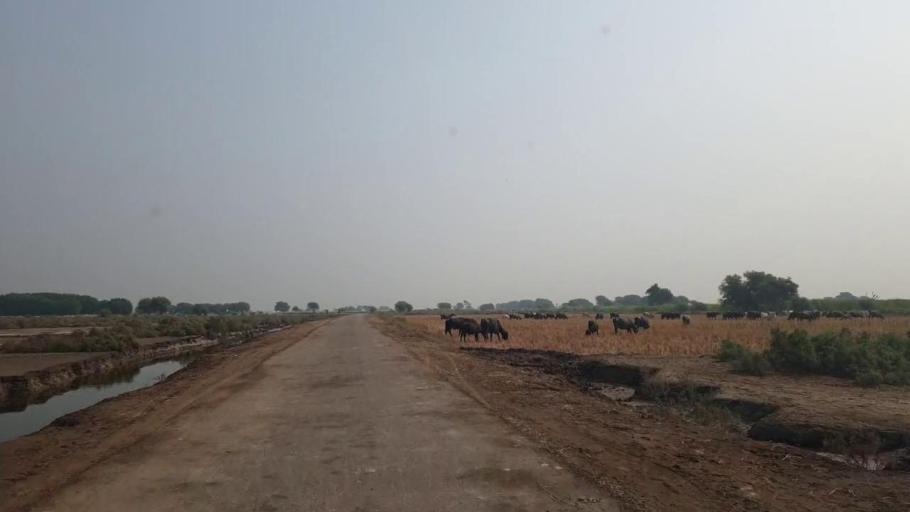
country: PK
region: Sindh
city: Matli
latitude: 25.1303
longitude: 68.6963
